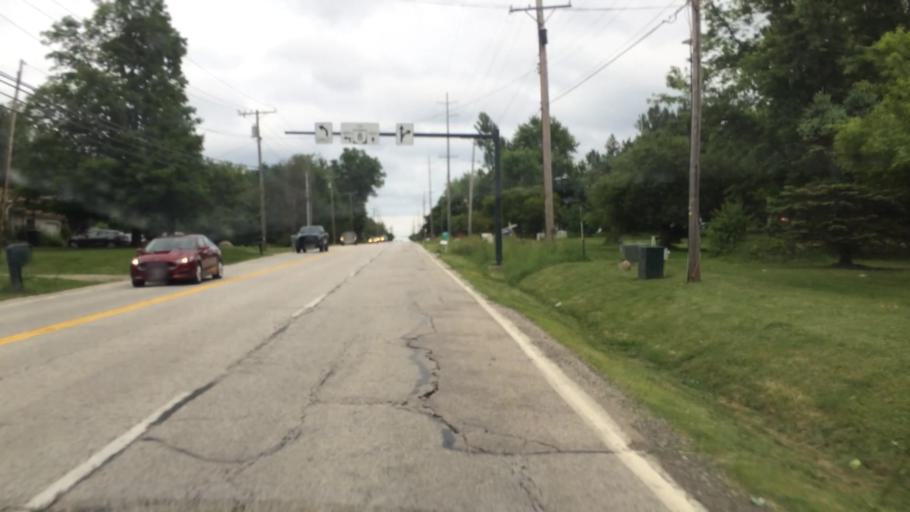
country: US
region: Ohio
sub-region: Summit County
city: Cuyahoga Falls
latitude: 41.1809
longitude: -81.5174
